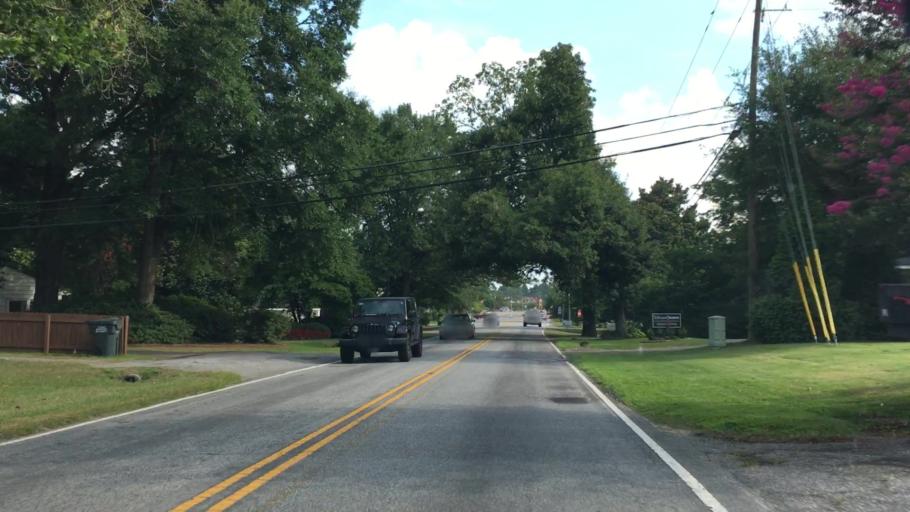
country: US
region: South Carolina
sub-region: Aiken County
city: Aiken
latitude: 33.5249
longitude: -81.7260
